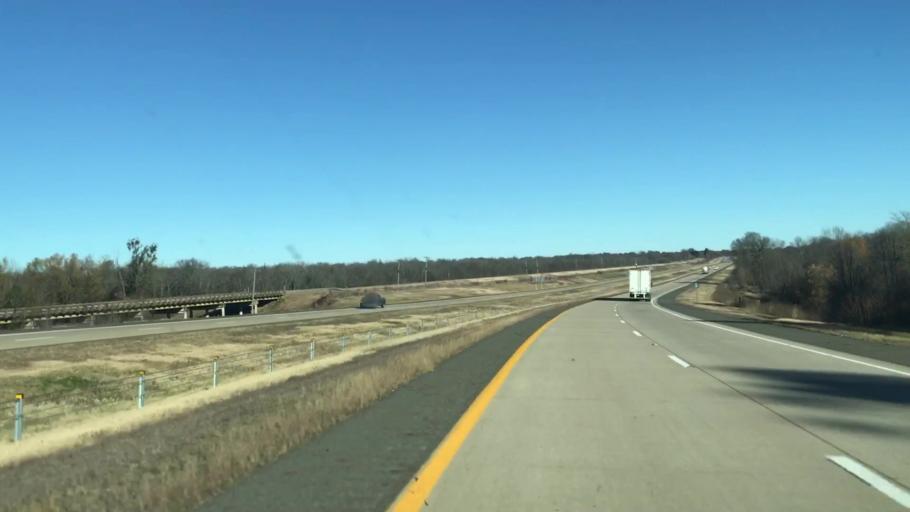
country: US
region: Texas
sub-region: Cass County
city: Queen City
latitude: 33.1347
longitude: -93.8951
